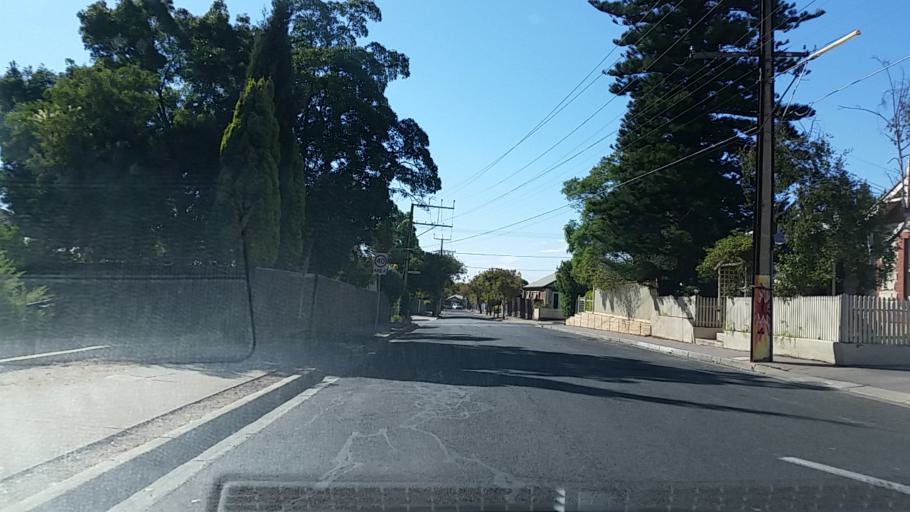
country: AU
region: South Australia
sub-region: Prospect
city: Prospect
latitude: -34.8836
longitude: 138.5893
